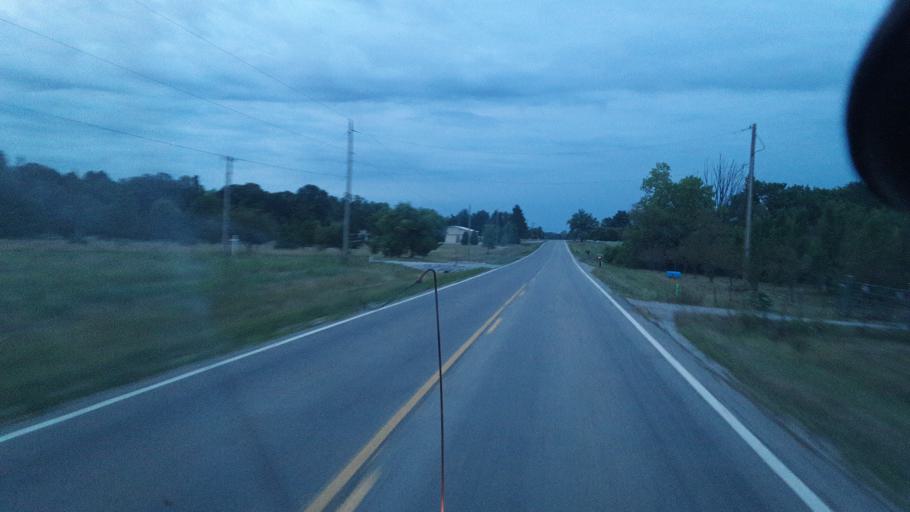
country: US
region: Ohio
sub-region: Defiance County
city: Hicksville
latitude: 41.3202
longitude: -84.7976
